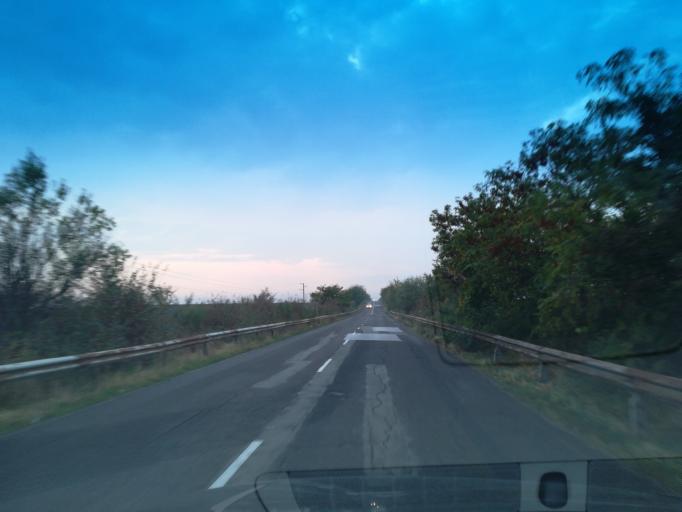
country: BG
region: Stara Zagora
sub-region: Obshtina Chirpan
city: Chirpan
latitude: 42.1937
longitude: 25.3014
